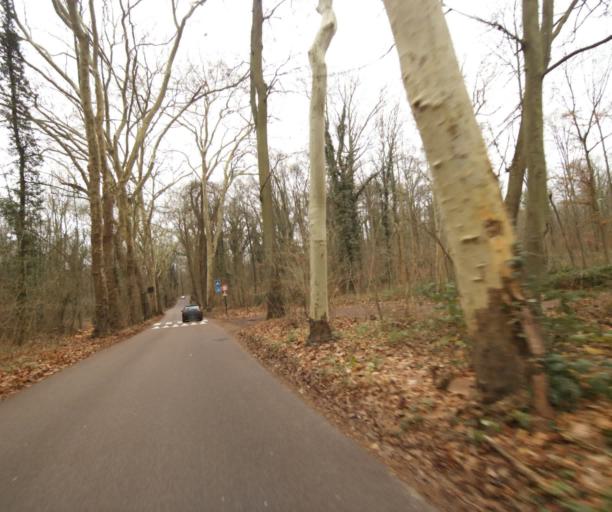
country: FR
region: Ile-de-France
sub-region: Departement des Hauts-de-Seine
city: Vaucresson
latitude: 48.8599
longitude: 2.1652
